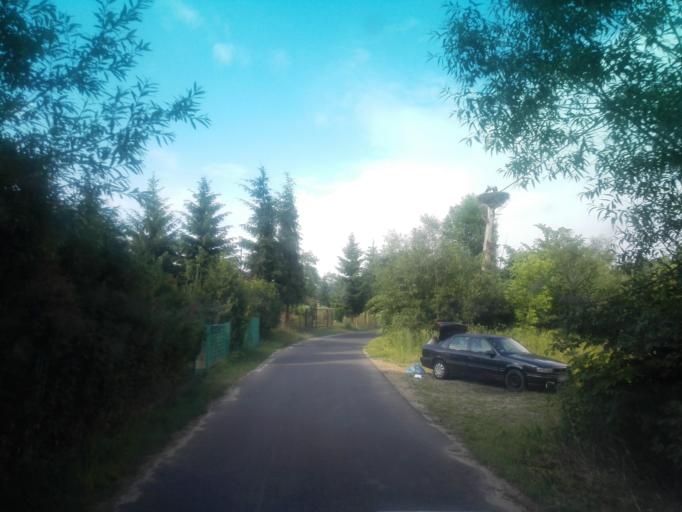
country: PL
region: Silesian Voivodeship
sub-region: Powiat czestochowski
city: Mstow
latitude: 50.8322
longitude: 19.3123
